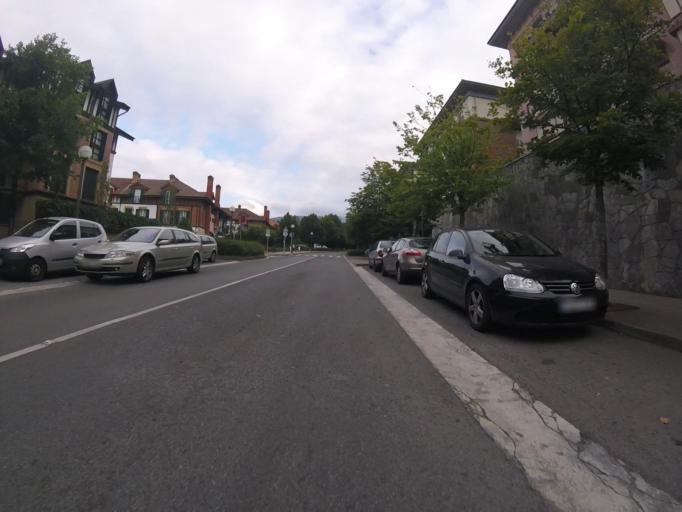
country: ES
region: Basque Country
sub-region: Provincia de Guipuzcoa
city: Irun
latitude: 43.3331
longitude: -1.7887
